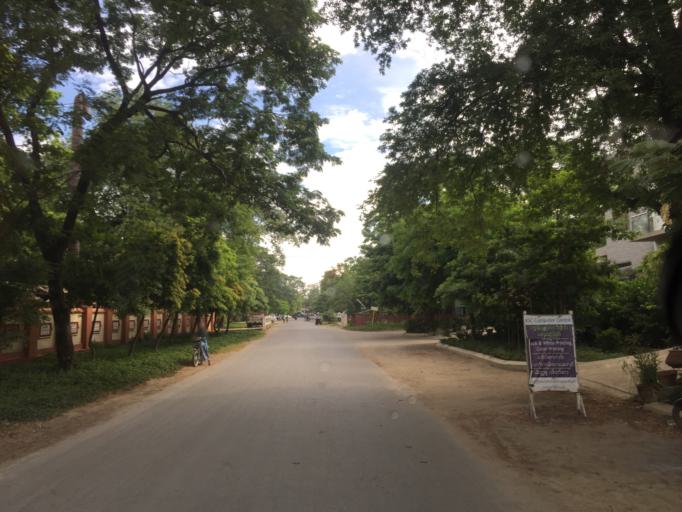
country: MM
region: Mandalay
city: Mandalay
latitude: 21.9736
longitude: 96.1047
